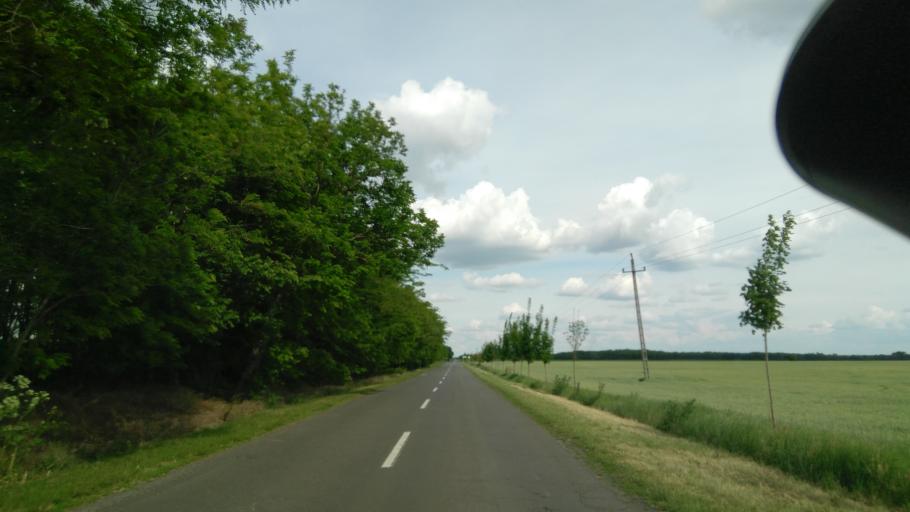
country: RO
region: Arad
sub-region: Comuna Peregu Mare
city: Peregu Mic
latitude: 46.3036
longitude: 20.9120
